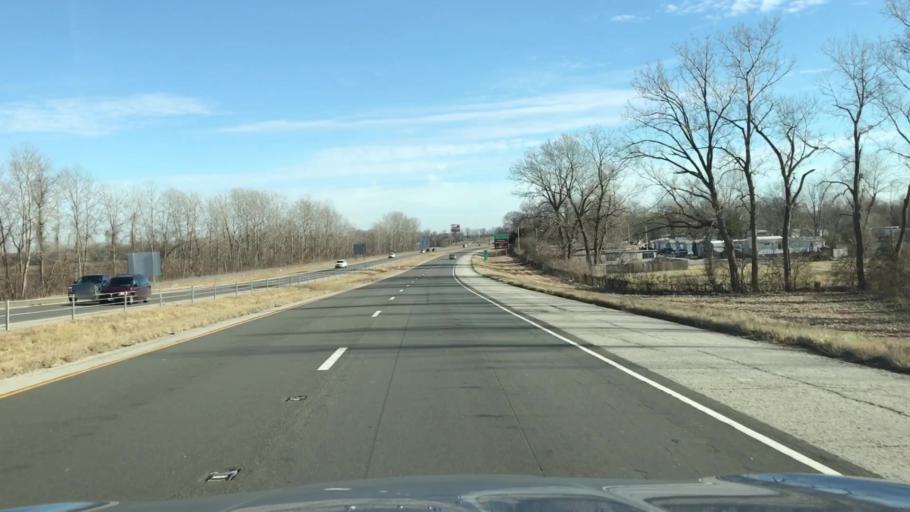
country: US
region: Illinois
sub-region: Madison County
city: Mitchell
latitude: 38.7650
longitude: -90.1106
